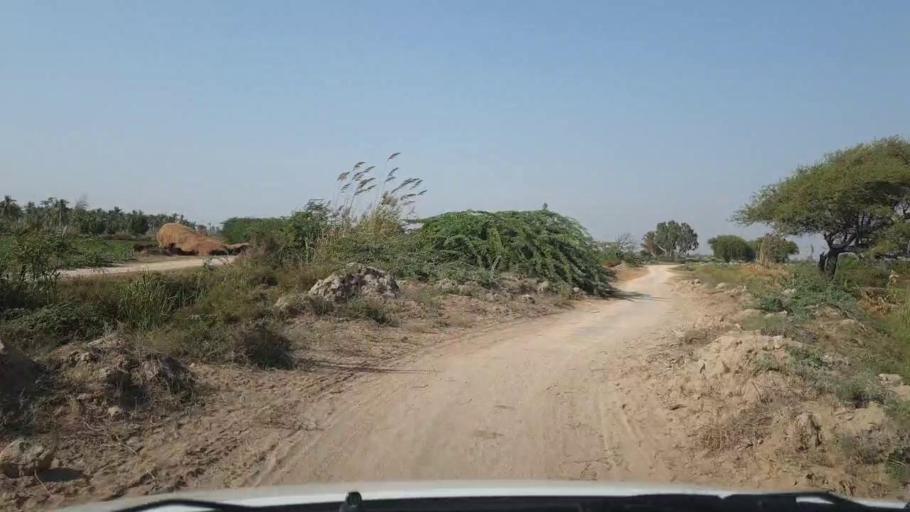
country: PK
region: Sindh
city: Mirpur Sakro
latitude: 24.5941
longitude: 67.6299
